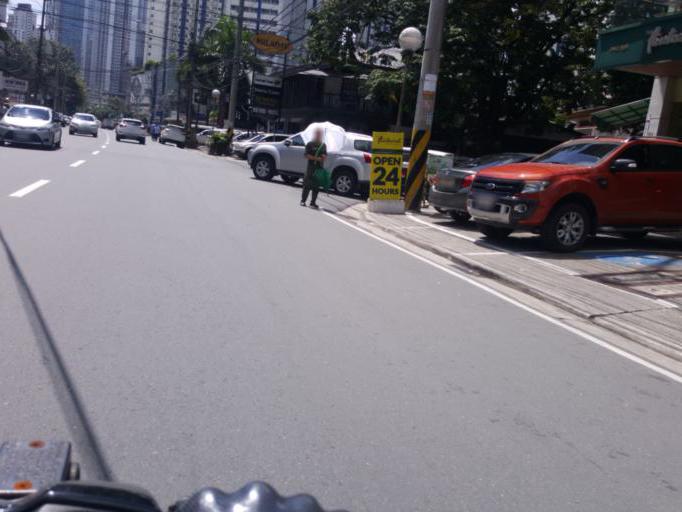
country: PH
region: Metro Manila
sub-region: Makati City
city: Makati City
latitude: 14.5629
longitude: 121.0241
